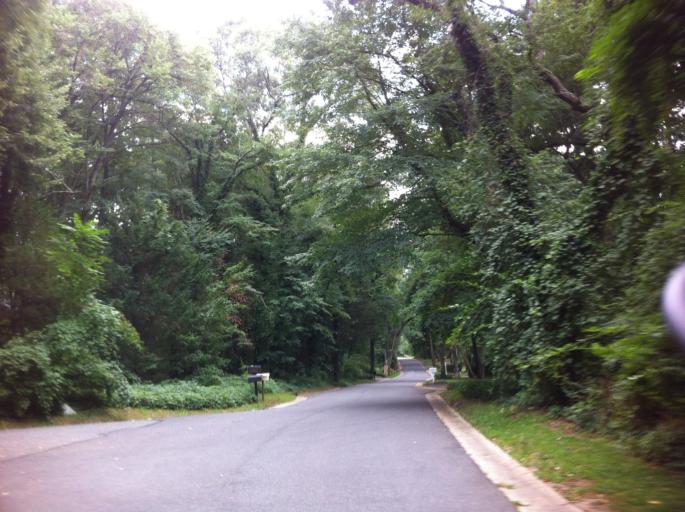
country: US
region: New York
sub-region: Nassau County
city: Old Brookville
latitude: 40.8368
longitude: -73.6054
